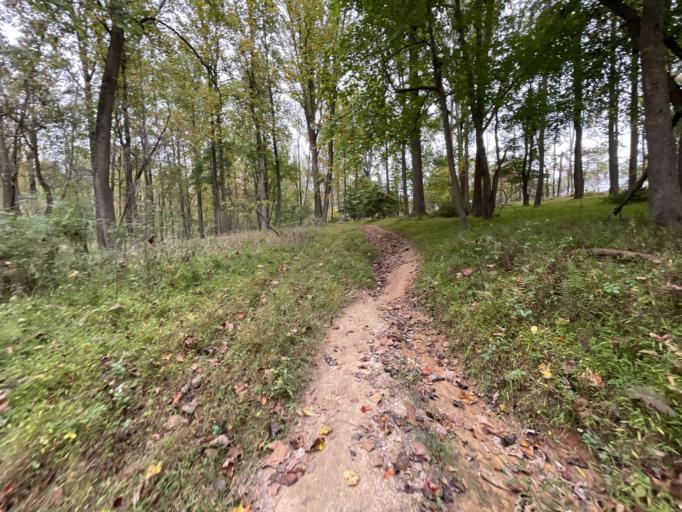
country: US
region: Maryland
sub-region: Baltimore County
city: Hampton
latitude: 39.4286
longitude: -76.5795
